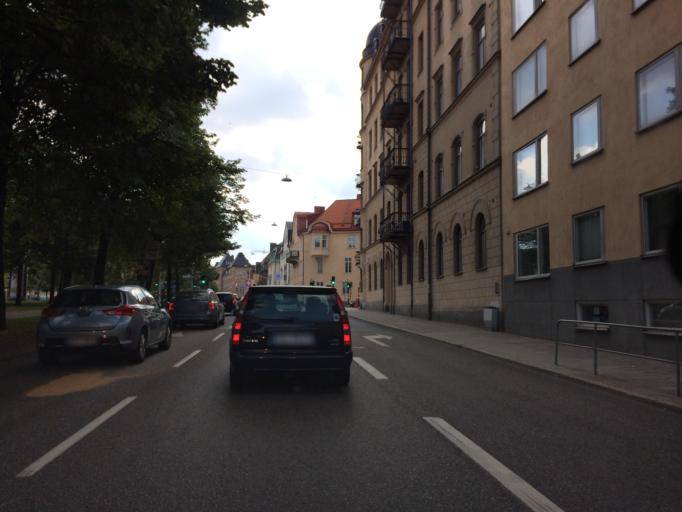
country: SE
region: Stockholm
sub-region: Stockholms Kommun
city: Stockholm
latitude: 59.3473
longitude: 18.0657
